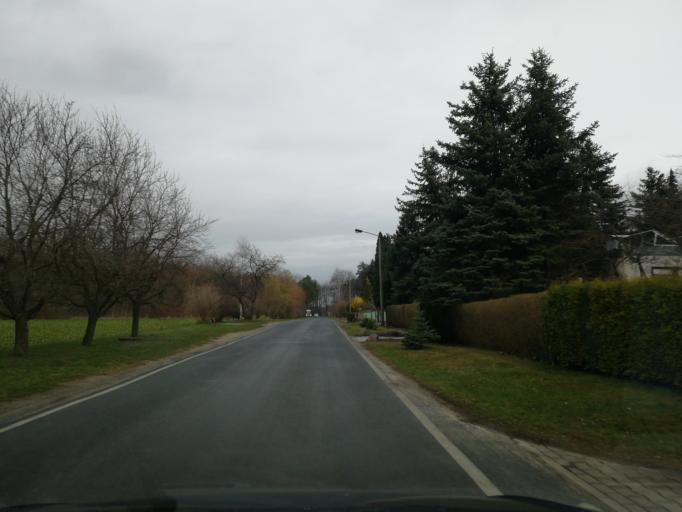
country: DE
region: Brandenburg
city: Calau
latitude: 51.7437
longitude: 13.9830
